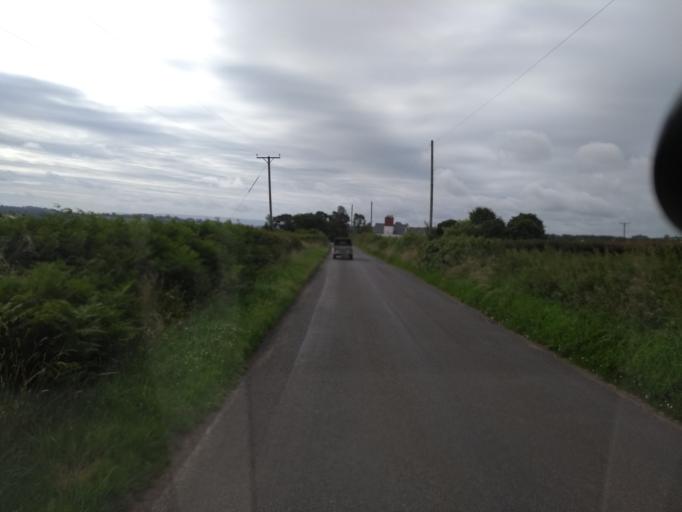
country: GB
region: England
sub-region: Somerset
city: Wiveliscombe
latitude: 51.0851
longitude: -3.2952
